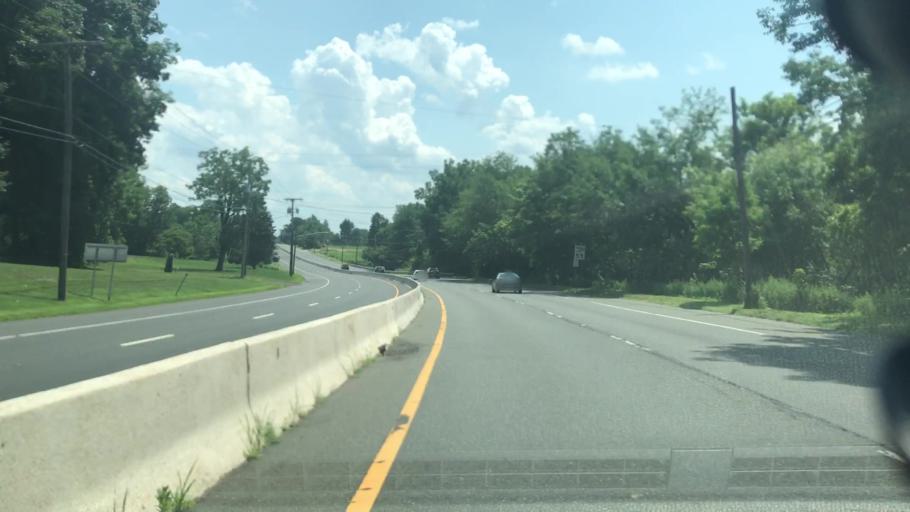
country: US
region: New Jersey
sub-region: Hunterdon County
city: Flemington
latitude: 40.4578
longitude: -74.8598
